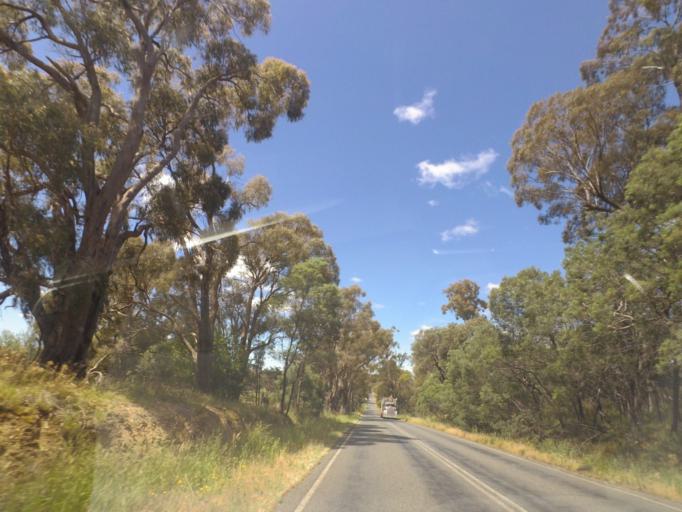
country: AU
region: Victoria
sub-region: Mount Alexander
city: Castlemaine
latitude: -37.3184
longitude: 144.2118
